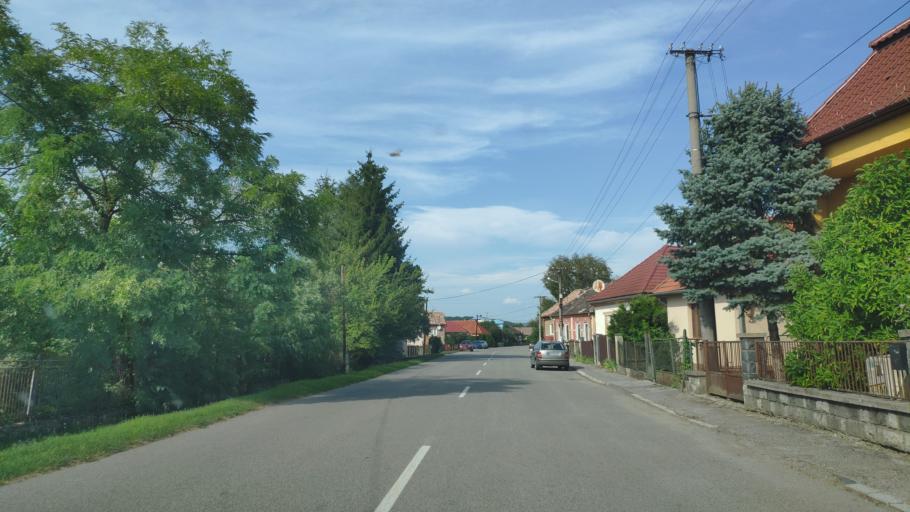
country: HU
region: Borsod-Abauj-Zemplen
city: Putnok
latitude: 48.4743
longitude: 20.3515
